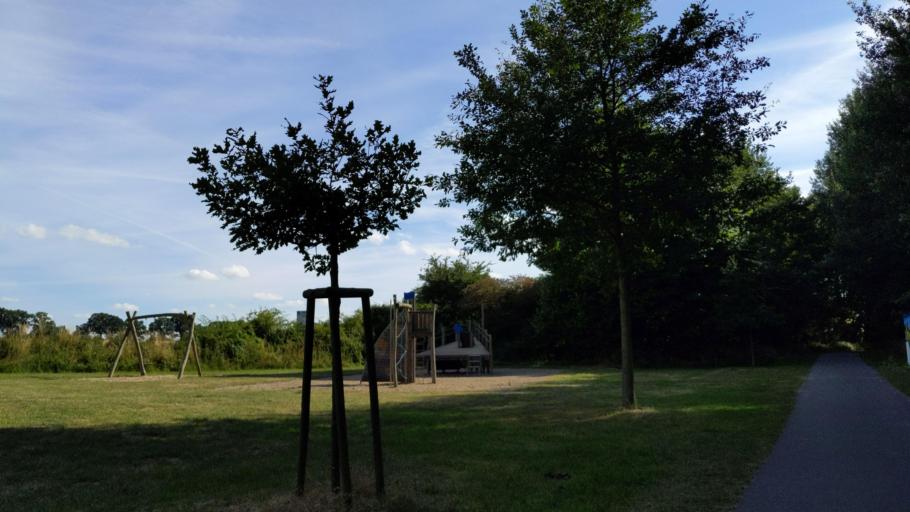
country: DE
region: Mecklenburg-Vorpommern
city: Kalkhorst
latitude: 53.9915
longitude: 10.9988
